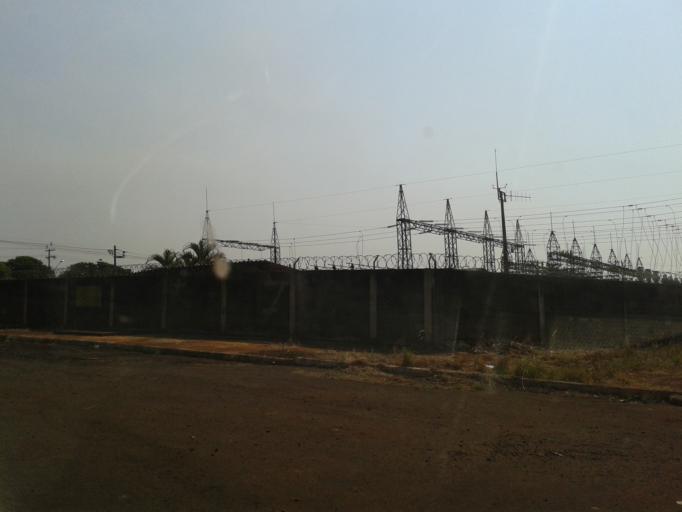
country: BR
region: Minas Gerais
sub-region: Ituiutaba
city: Ituiutaba
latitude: -18.9638
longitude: -49.4480
